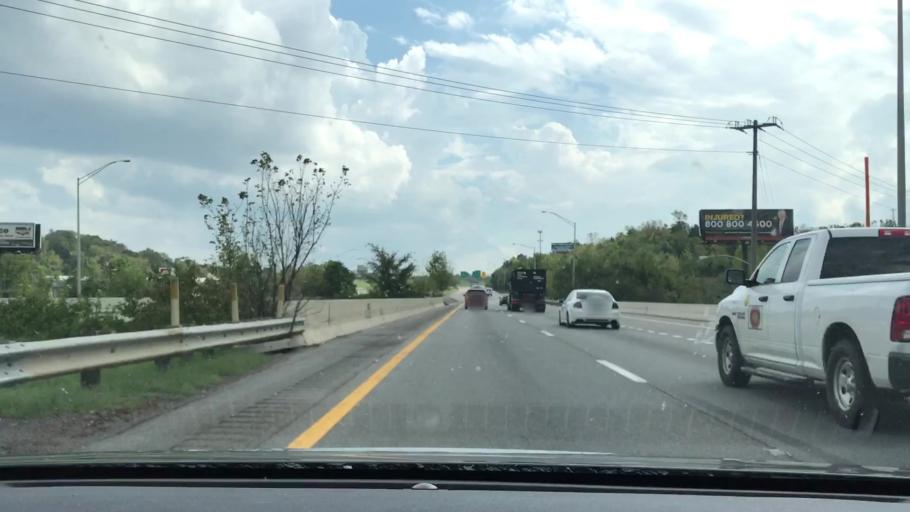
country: US
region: Tennessee
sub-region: Davidson County
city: Nashville
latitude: 36.2304
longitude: -86.7820
